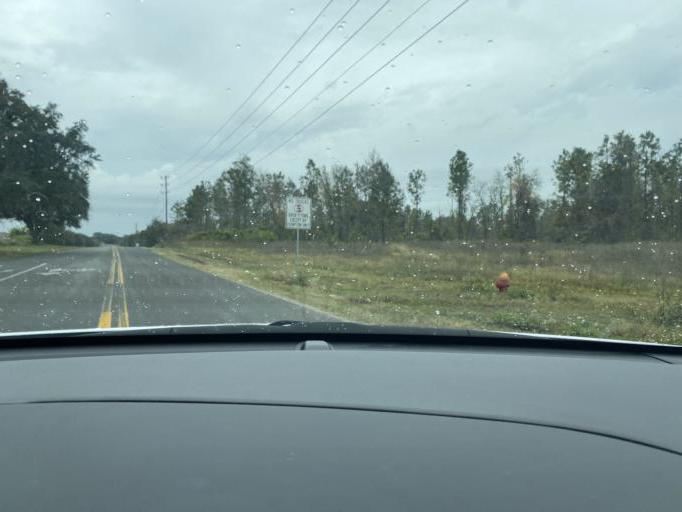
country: US
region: Florida
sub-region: Lake County
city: Mascotte
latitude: 28.5842
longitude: -81.8723
